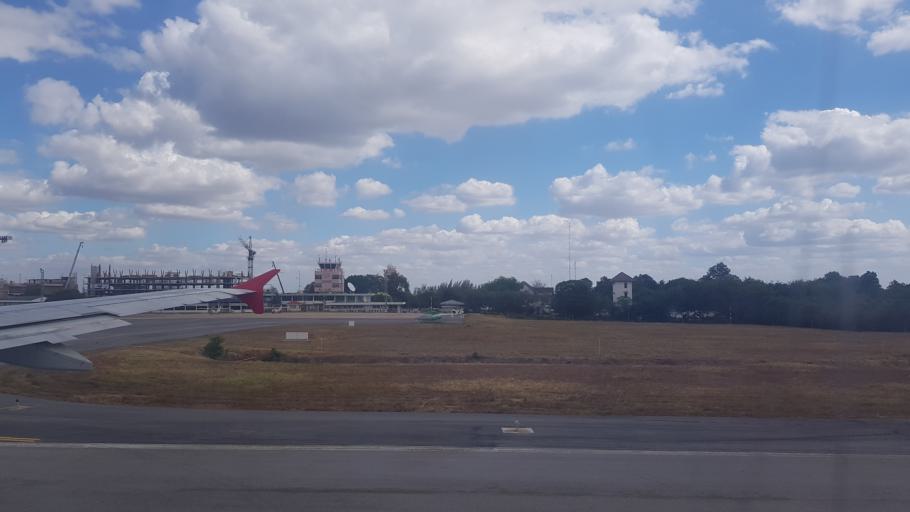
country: TH
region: Khon Kaen
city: Khon Kaen
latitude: 16.4635
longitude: 102.7816
